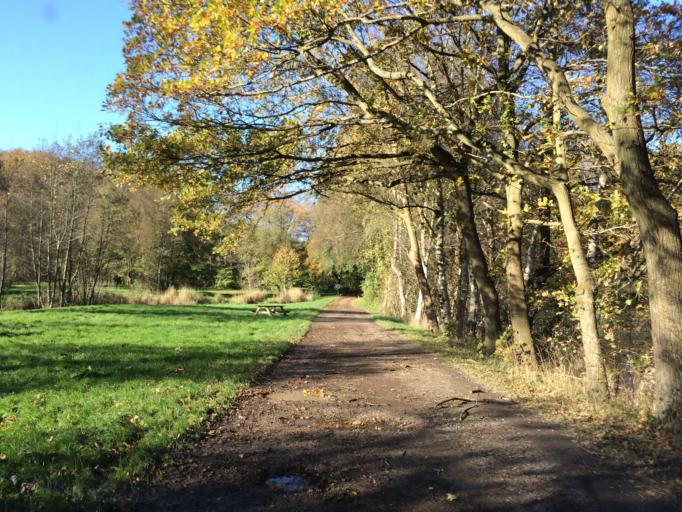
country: DK
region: South Denmark
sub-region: Fredericia Kommune
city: Taulov
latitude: 55.5693
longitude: 9.6299
